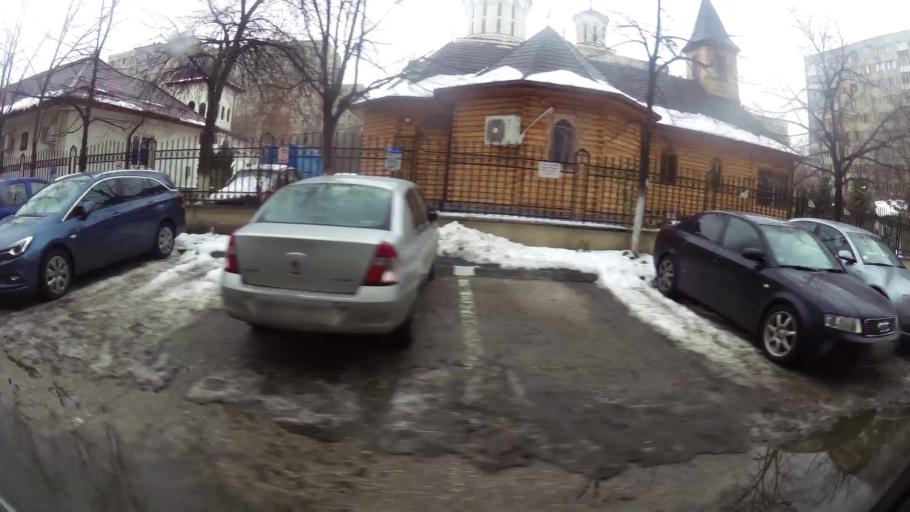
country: RO
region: Ilfov
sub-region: Comuna Chiajna
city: Rosu
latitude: 44.4207
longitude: 26.0280
